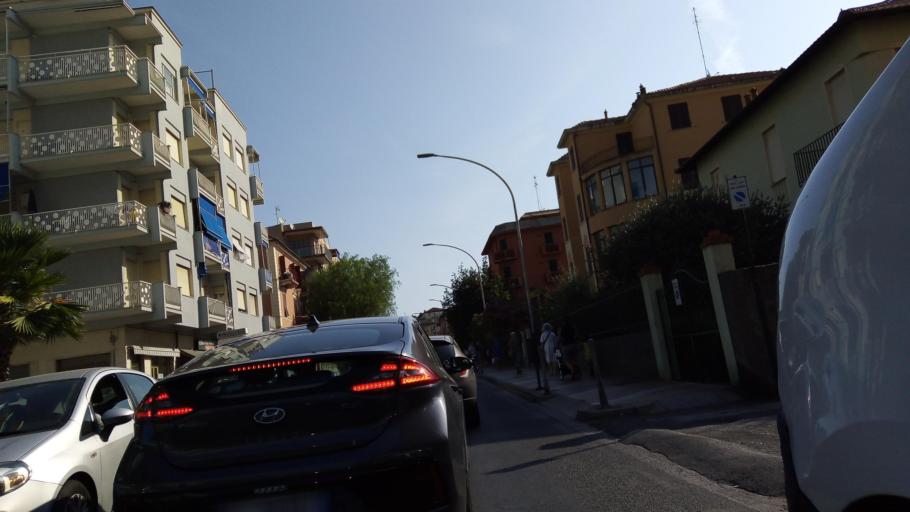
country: IT
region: Liguria
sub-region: Provincia di Savona
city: Loano
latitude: 44.1224
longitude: 8.2526
